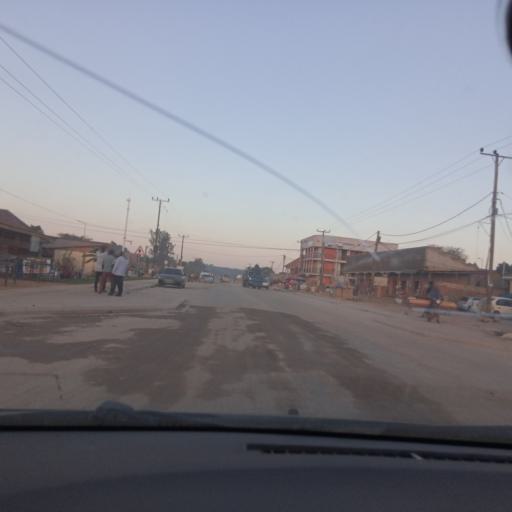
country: UG
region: Central Region
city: Masaka
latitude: -0.3238
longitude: 31.7603
